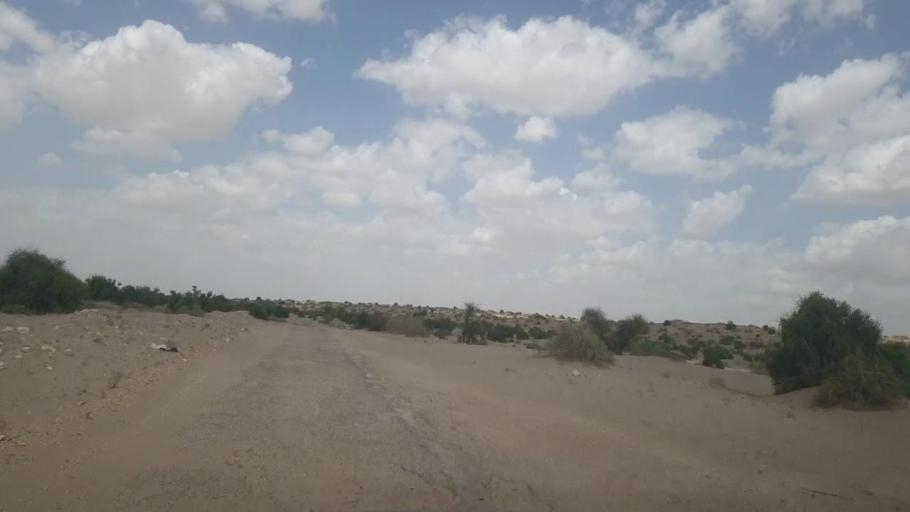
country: PK
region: Sindh
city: Kot Diji
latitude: 27.2734
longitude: 69.2153
